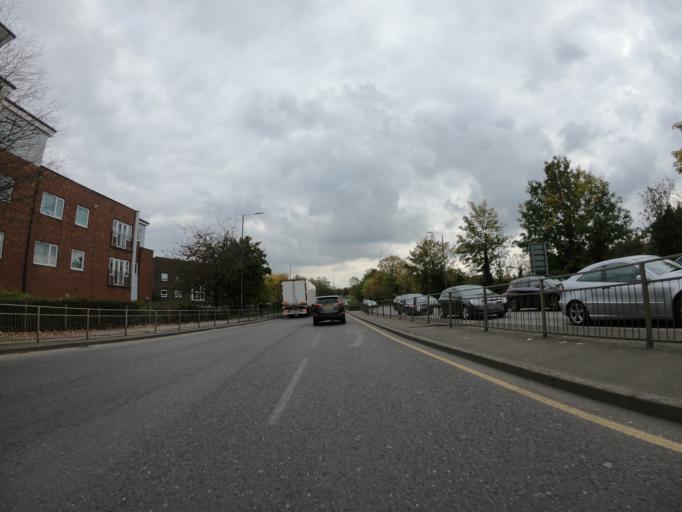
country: GB
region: England
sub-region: Greater London
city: Erith
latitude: 51.4780
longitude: 0.1801
